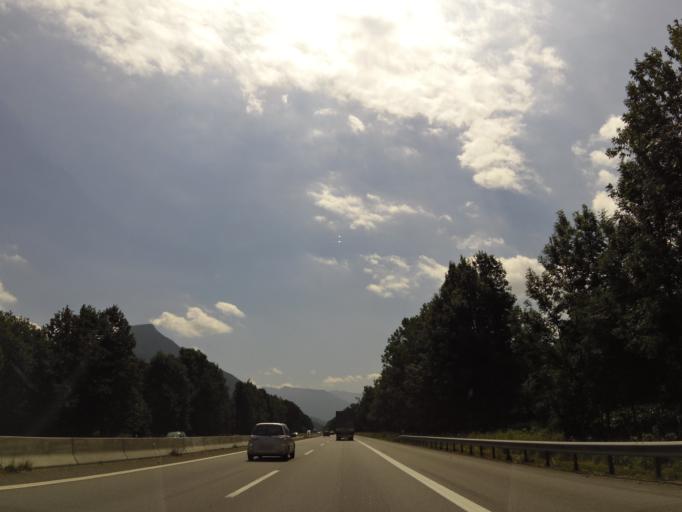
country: DE
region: Bavaria
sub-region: Upper Bavaria
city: Flintsbach
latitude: 47.7241
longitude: 12.1385
